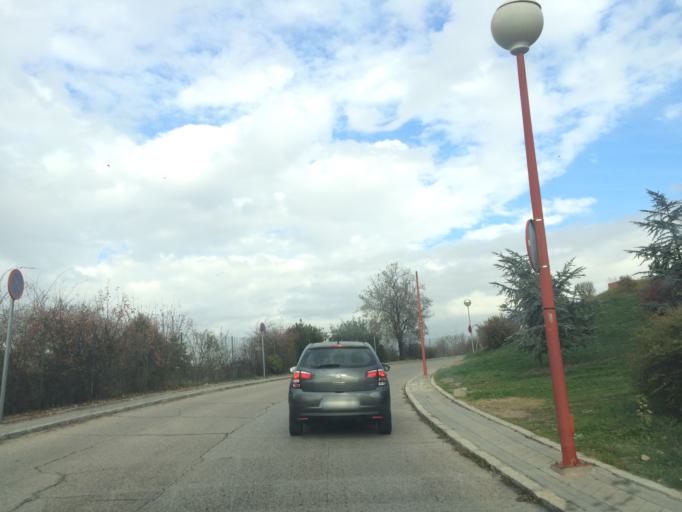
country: ES
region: Madrid
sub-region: Provincia de Madrid
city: Moncloa-Aravaca
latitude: 40.4469
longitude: -3.7376
